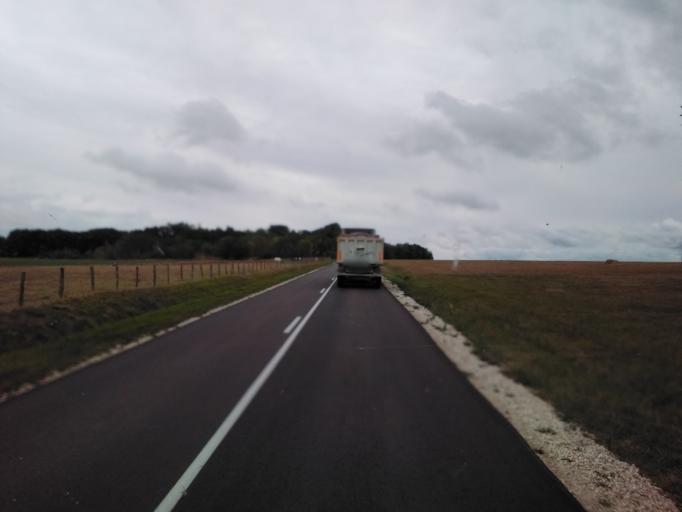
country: FR
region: Champagne-Ardenne
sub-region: Departement de l'Aube
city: Vendeuvre-sur-Barse
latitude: 48.3070
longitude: 4.5206
